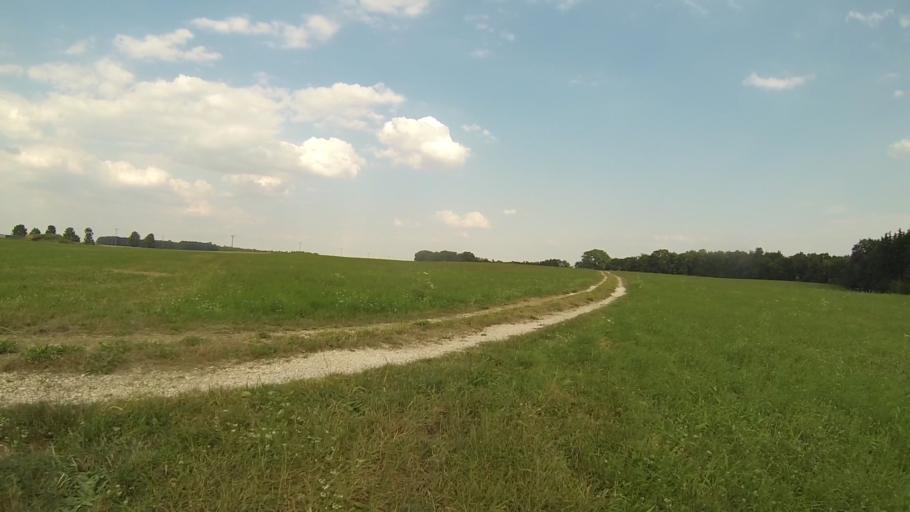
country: DE
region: Baden-Wuerttemberg
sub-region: Tuebingen Region
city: Blaubeuren
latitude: 48.4532
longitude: 9.8527
